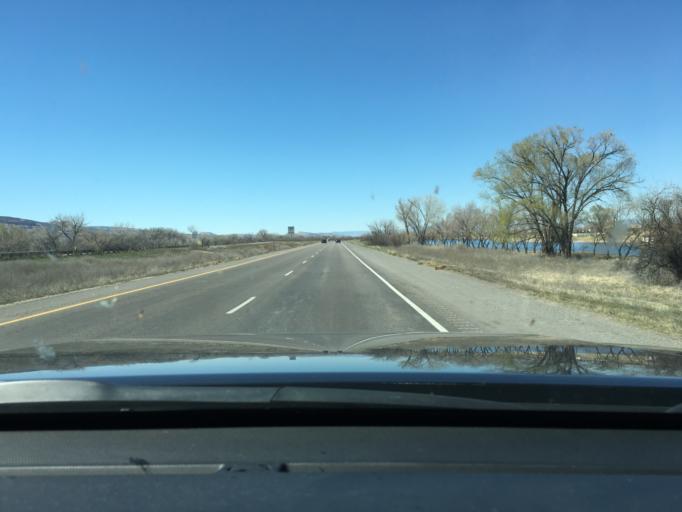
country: US
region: Colorado
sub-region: Mesa County
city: Redlands
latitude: 39.1178
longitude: -108.6689
